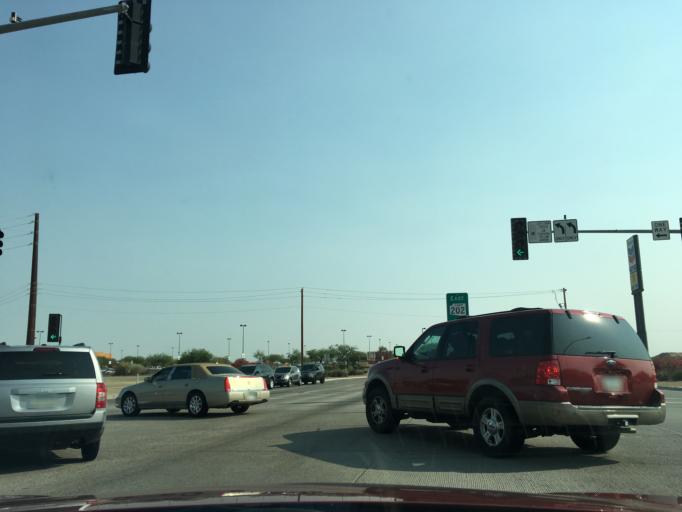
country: US
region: Arizona
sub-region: Maricopa County
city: Guadalupe
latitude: 33.2918
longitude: -111.9457
